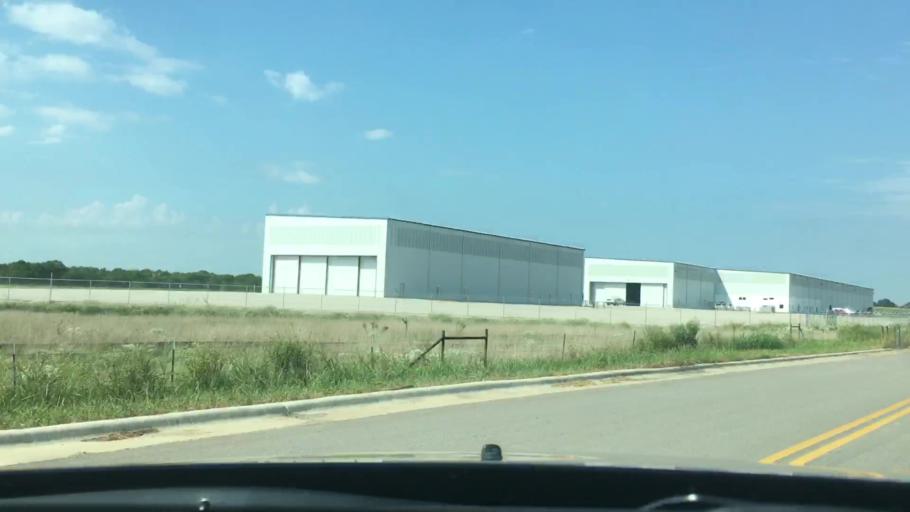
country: US
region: Oklahoma
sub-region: Bryan County
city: Durant
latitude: 33.9687
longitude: -96.3609
